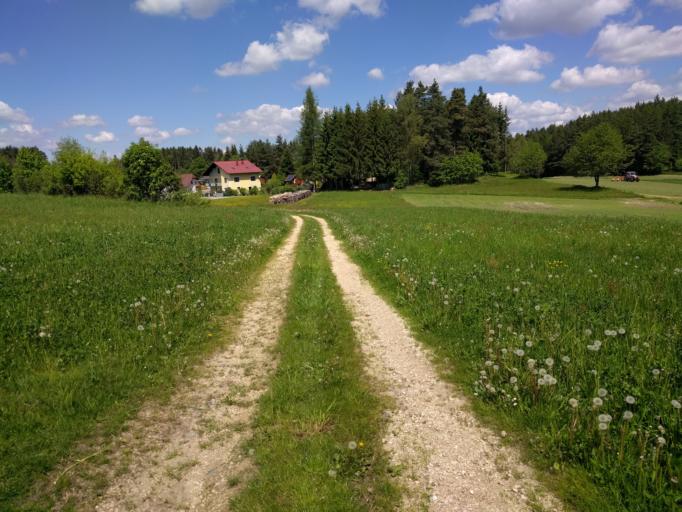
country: AT
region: Lower Austria
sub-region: Politischer Bezirk Zwettl
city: Langschlag
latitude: 48.5869
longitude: 14.8994
